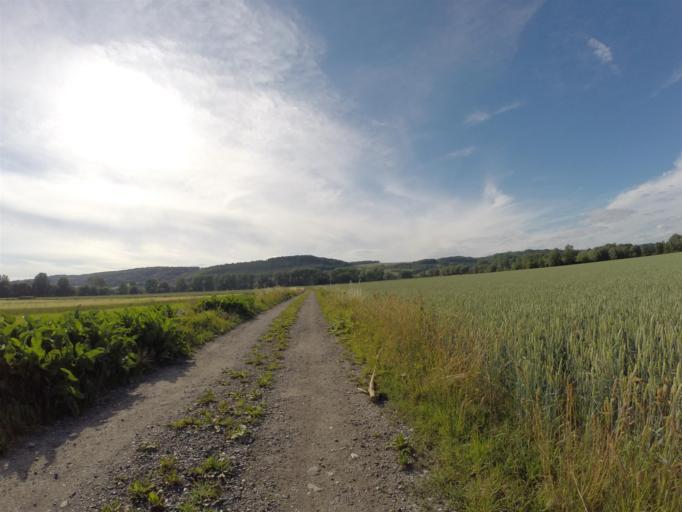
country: DE
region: Thuringia
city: Golmsdorf
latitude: 50.9760
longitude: 11.6674
